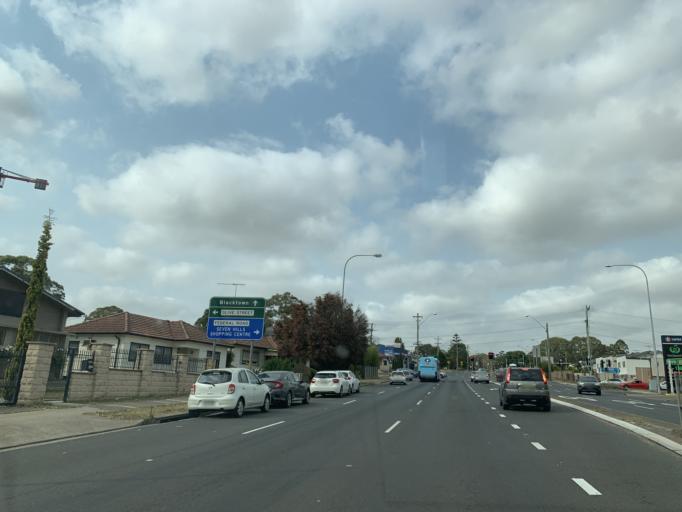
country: AU
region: New South Wales
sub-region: Blacktown
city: Blacktown
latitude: -33.7761
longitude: 150.9338
